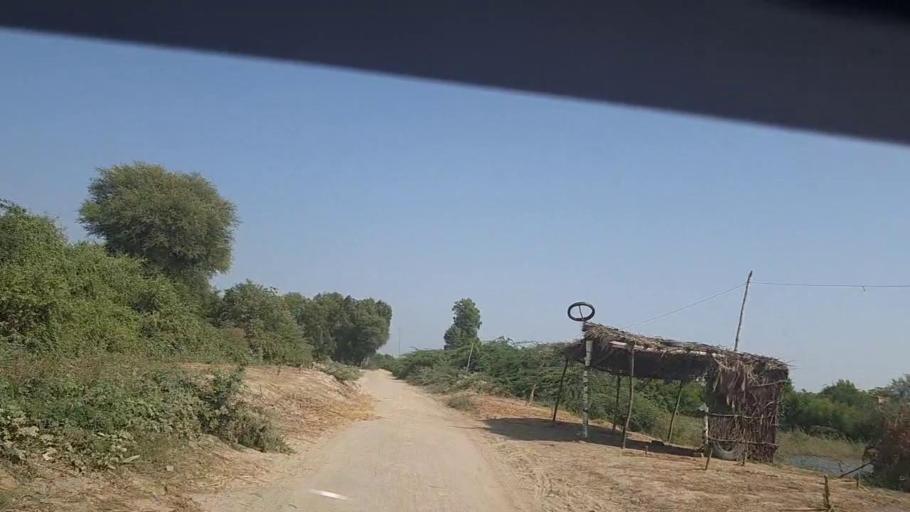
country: PK
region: Sindh
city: Rajo Khanani
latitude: 24.9692
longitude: 68.8770
